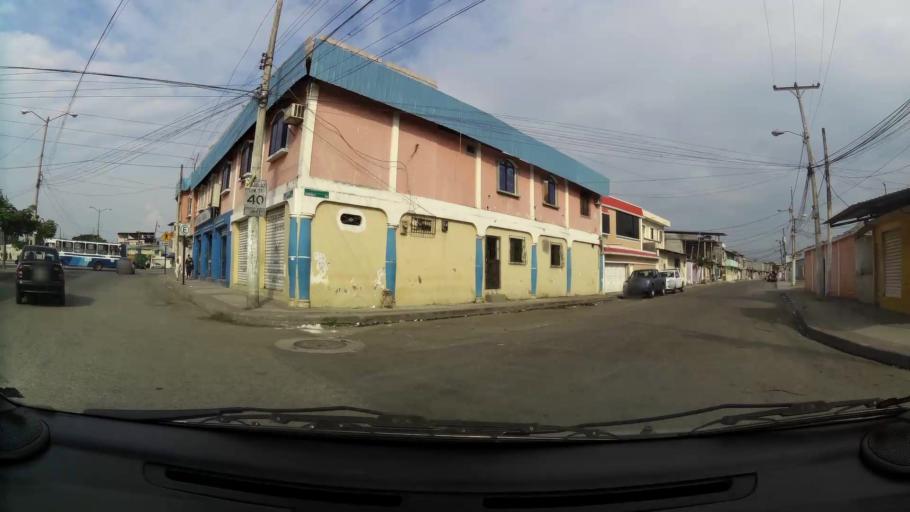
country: EC
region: Guayas
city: Guayaquil
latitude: -2.2453
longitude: -79.9051
